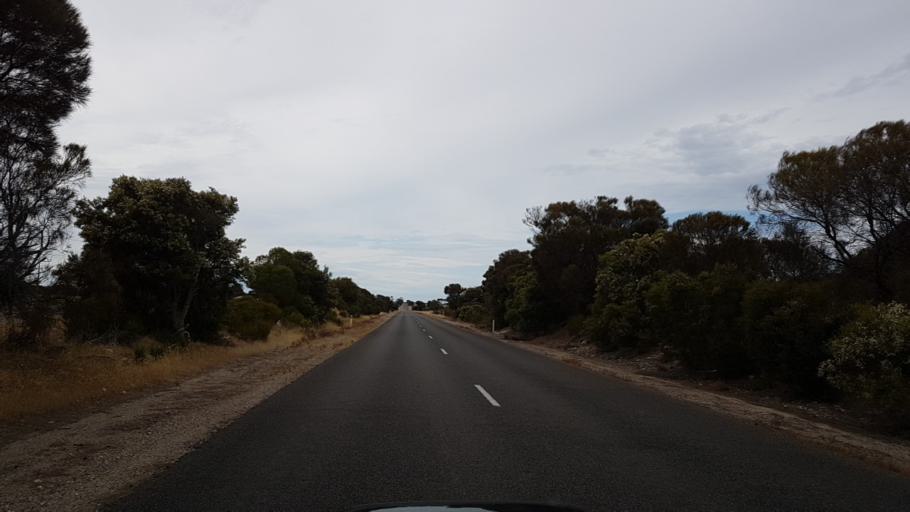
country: AU
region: South Australia
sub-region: Yorke Peninsula
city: Honiton
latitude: -34.9360
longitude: 137.0901
